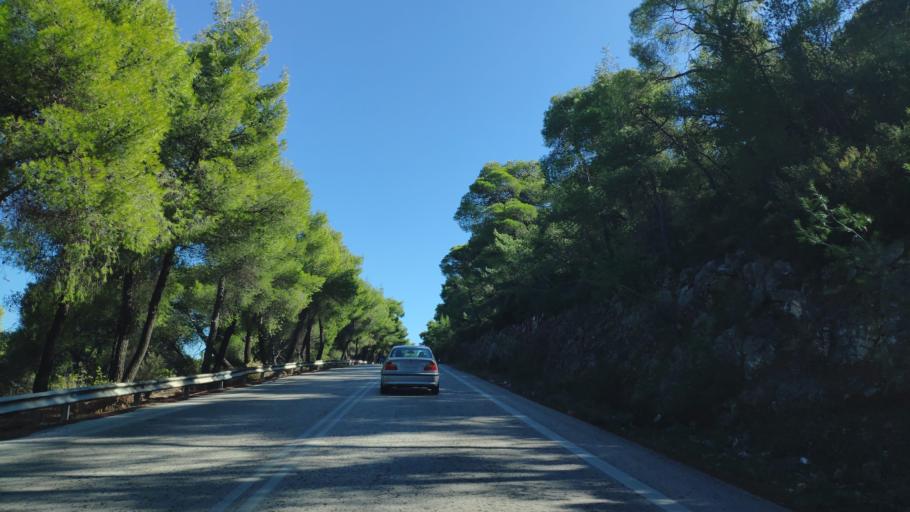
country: GR
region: Peloponnese
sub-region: Nomos Korinthias
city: Sofikon
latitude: 37.8264
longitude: 23.0968
